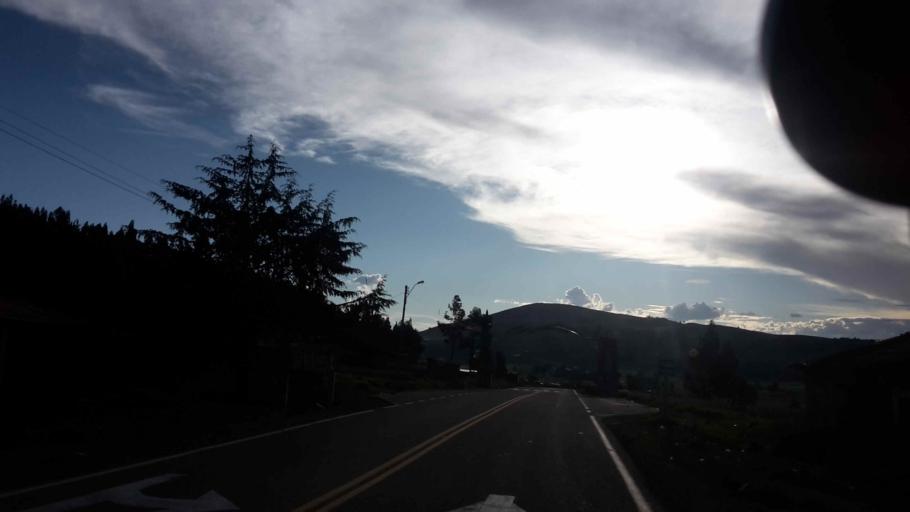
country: BO
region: Cochabamba
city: Arani
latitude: -17.5473
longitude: -65.6728
